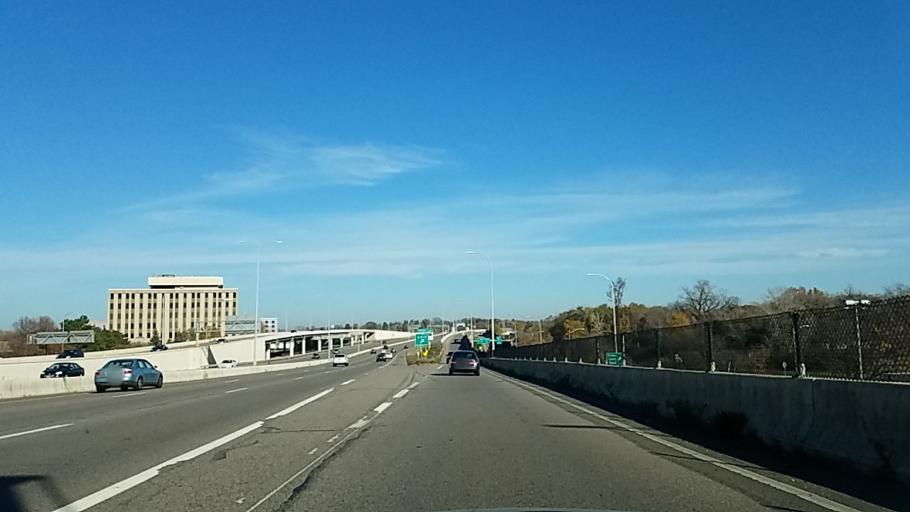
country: US
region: Minnesota
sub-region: Hennepin County
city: Saint Louis Park
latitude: 44.9633
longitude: -93.3438
